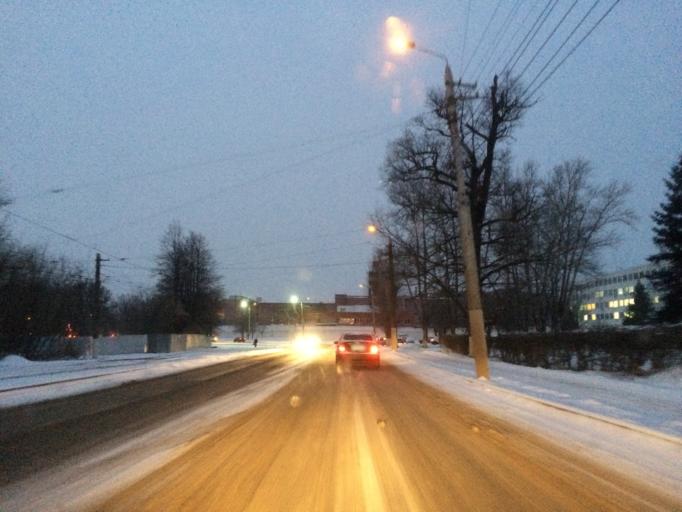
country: RU
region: Tula
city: Tula
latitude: 54.2209
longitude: 37.6891
